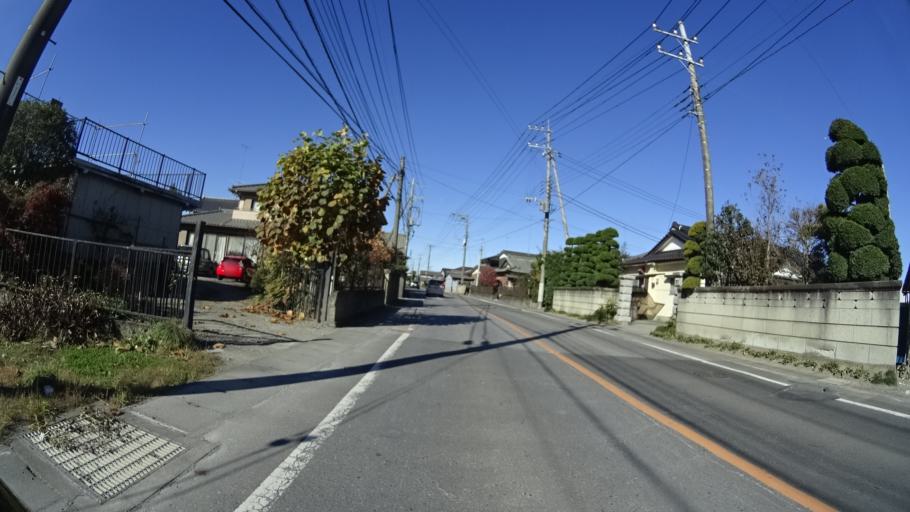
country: JP
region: Tochigi
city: Mibu
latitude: 36.4497
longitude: 139.7564
